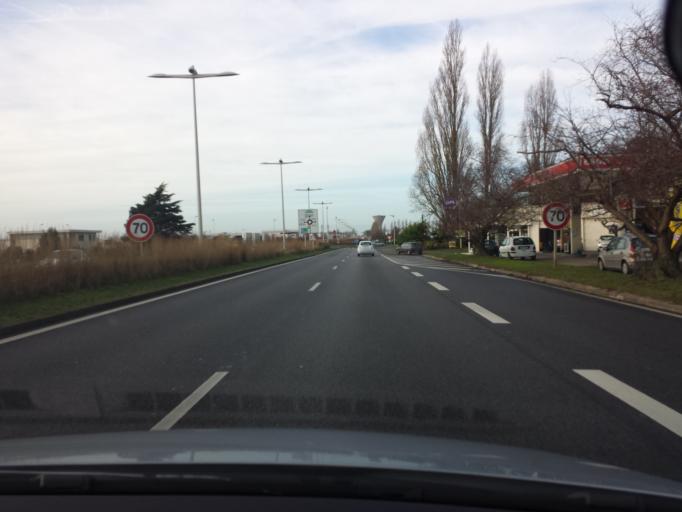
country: FR
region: Haute-Normandie
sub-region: Departement de l'Eure
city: Evreux
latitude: 49.0154
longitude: 1.1897
